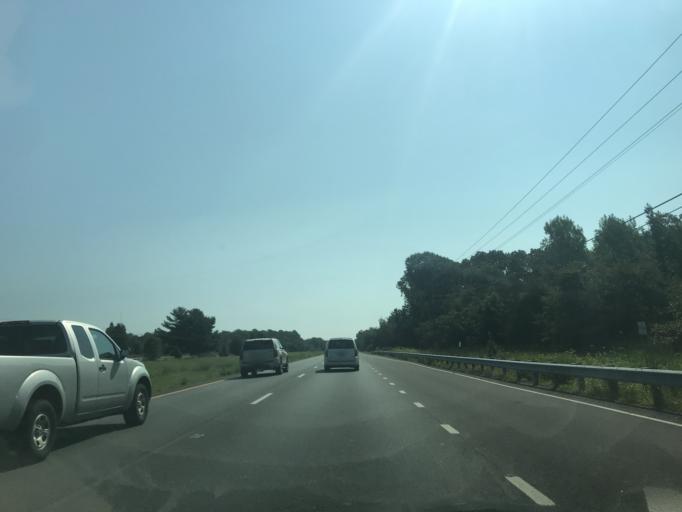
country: US
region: Maryland
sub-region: Charles County
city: Hughesville
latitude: 38.5504
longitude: -76.8189
